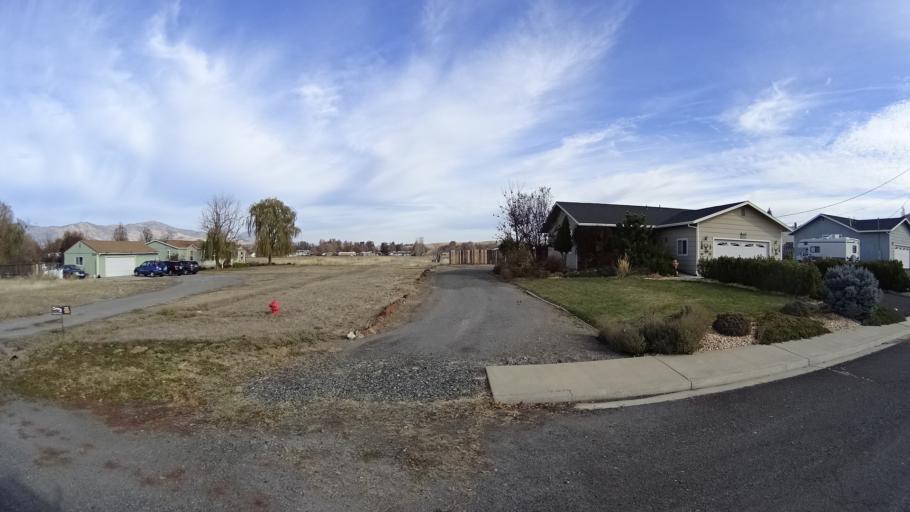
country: US
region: California
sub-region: Siskiyou County
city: Montague
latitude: 41.7207
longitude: -122.5239
